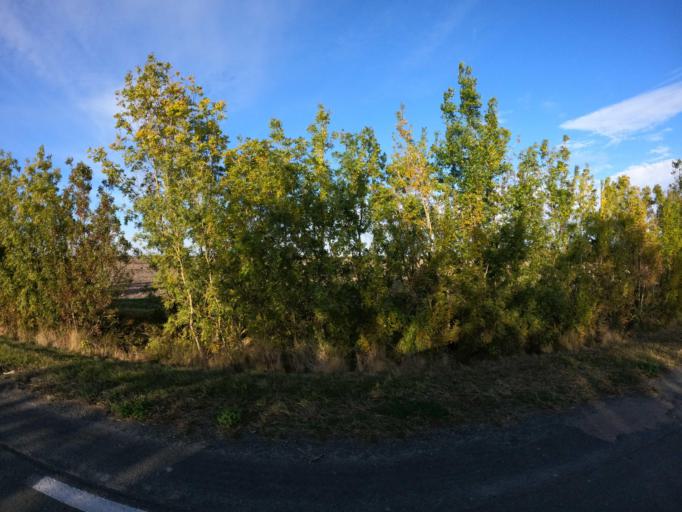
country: FR
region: Pays de la Loire
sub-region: Departement de la Vendee
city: Chaille-les-Marais
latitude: 46.4112
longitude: -1.0400
